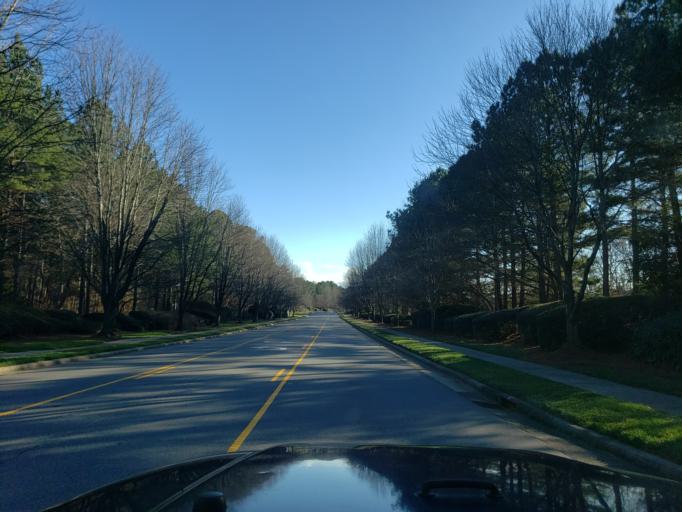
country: US
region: North Carolina
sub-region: Catawba County
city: Lake Norman of Catawba
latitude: 35.5419
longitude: -80.9172
